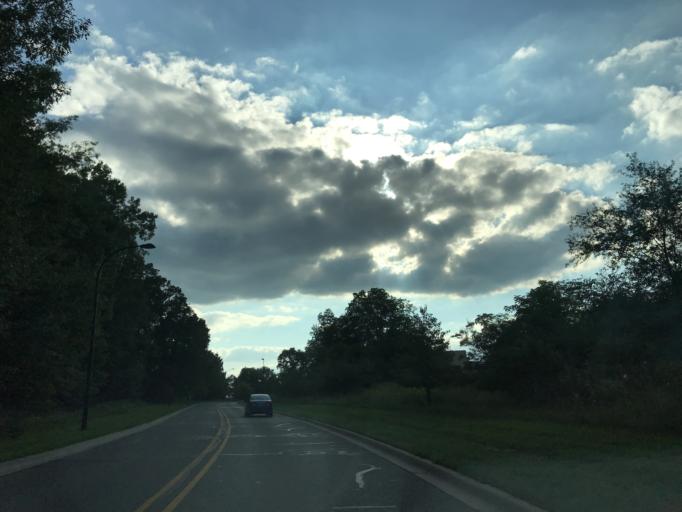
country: US
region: Michigan
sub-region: Washtenaw County
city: Ann Arbor
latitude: 42.2980
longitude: -83.6994
